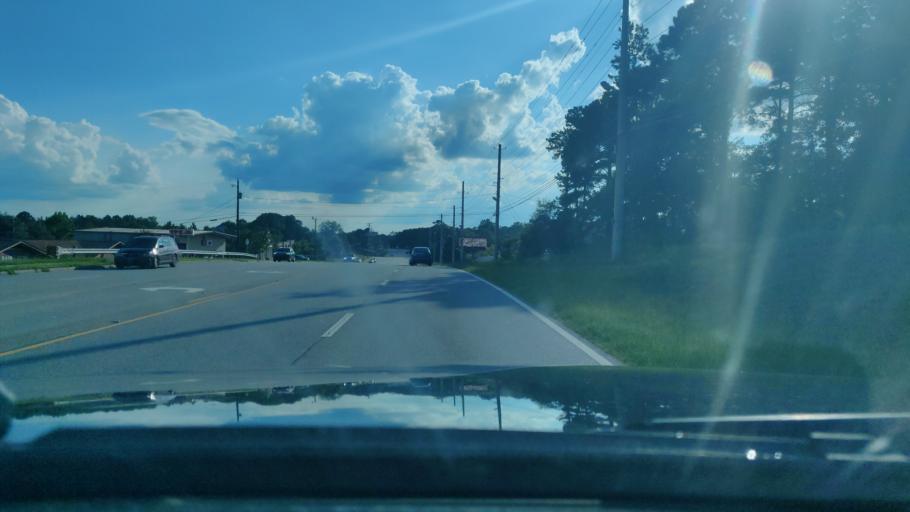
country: US
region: Alabama
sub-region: Lee County
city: Opelika
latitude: 32.6218
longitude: -85.4127
